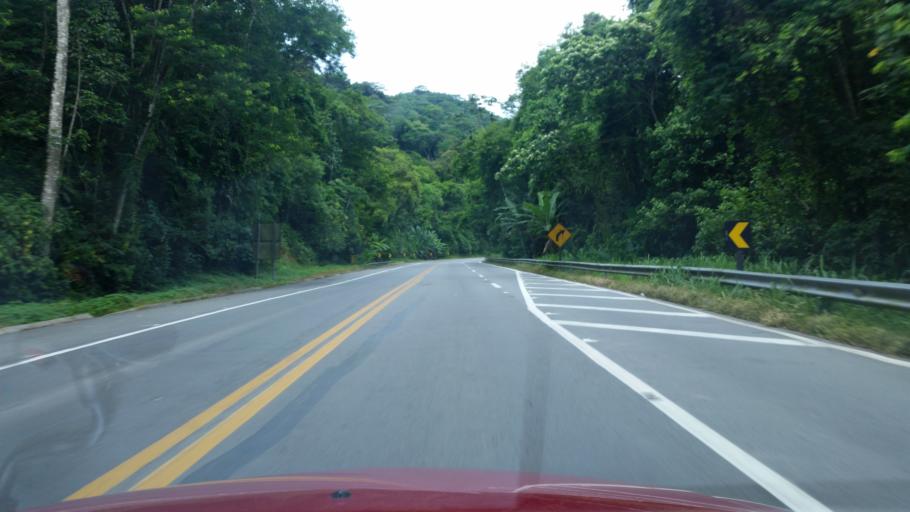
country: BR
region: Sao Paulo
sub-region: Miracatu
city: Miracatu
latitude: -24.2656
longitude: -47.2952
